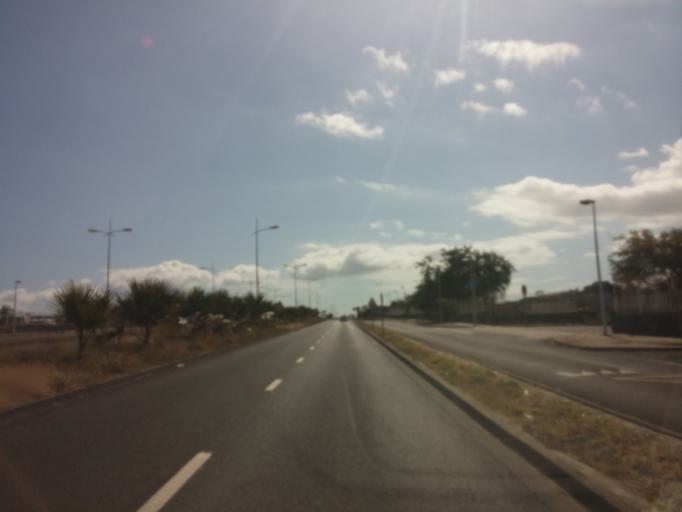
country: RE
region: Reunion
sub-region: Reunion
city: Le Port
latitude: -20.9673
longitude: 55.2953
